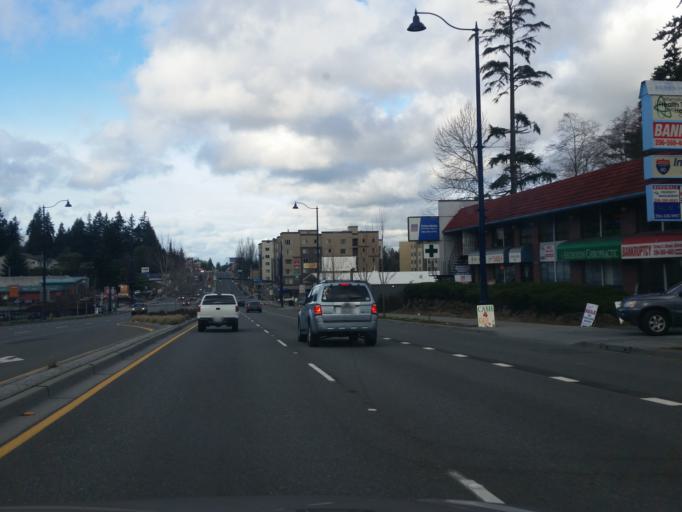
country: US
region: Washington
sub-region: King County
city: Shoreline
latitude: 47.7661
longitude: -122.3459
